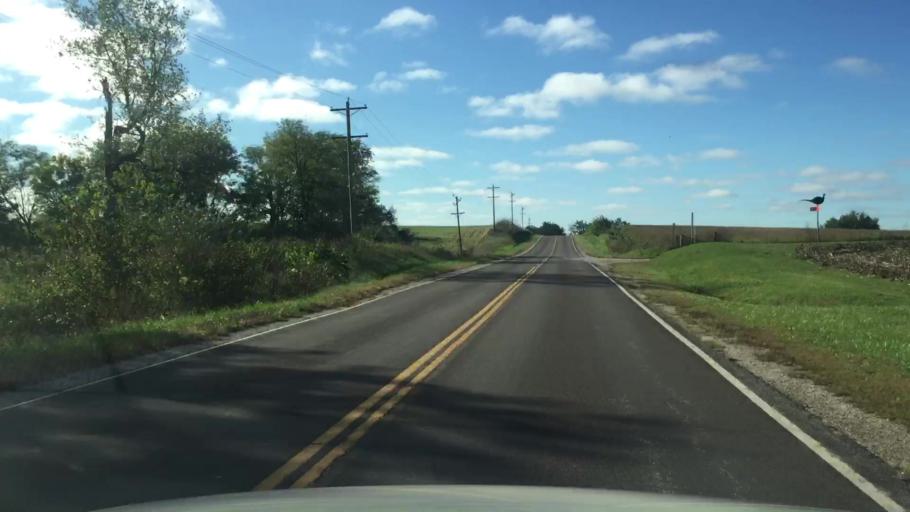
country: US
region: Missouri
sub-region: Howard County
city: New Franklin
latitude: 39.0686
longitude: -92.7460
